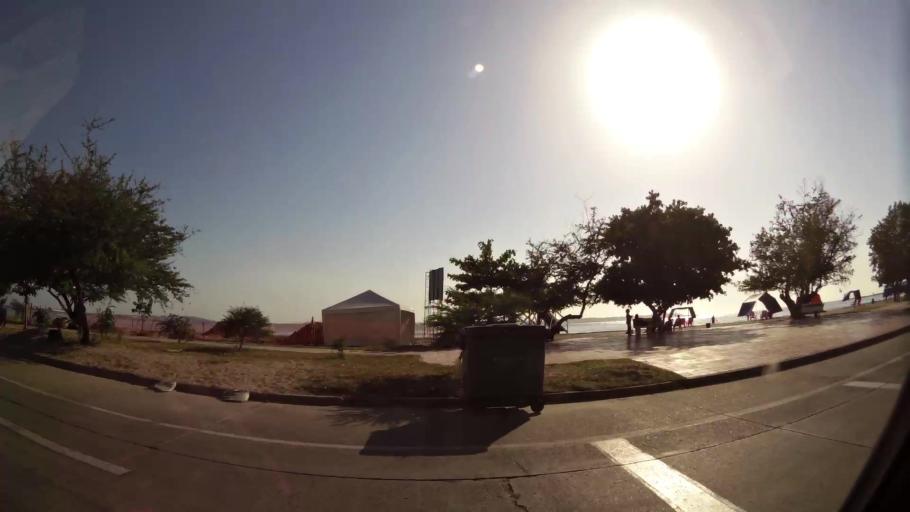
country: CO
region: Bolivar
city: Cartagena
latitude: 10.3928
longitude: -75.5509
